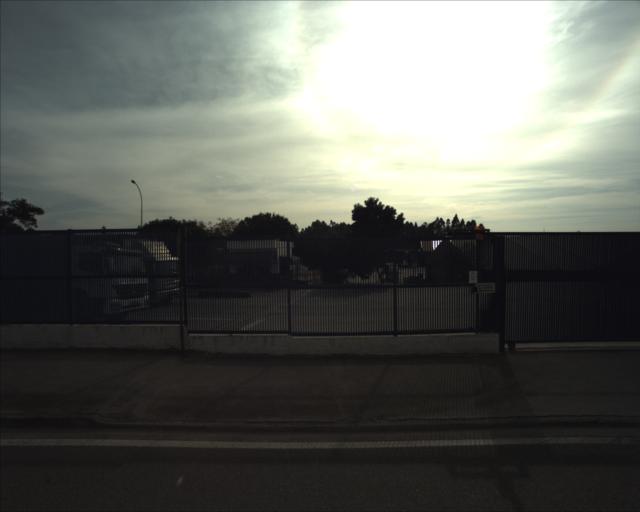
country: BR
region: Sao Paulo
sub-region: Sorocaba
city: Sorocaba
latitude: -23.4646
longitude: -47.4301
